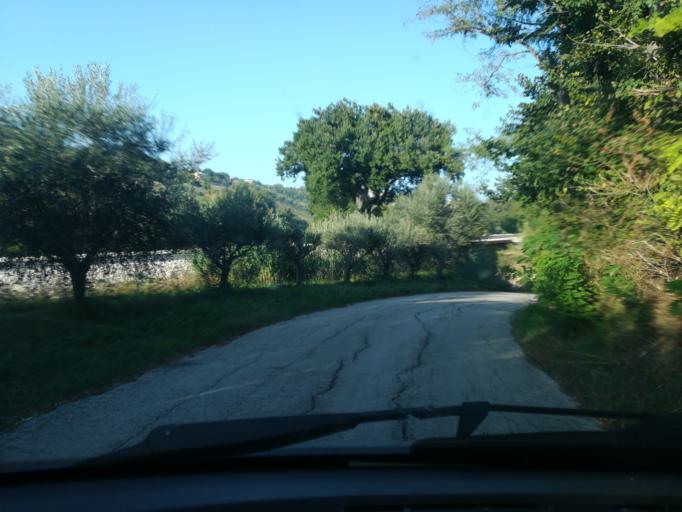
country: IT
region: The Marches
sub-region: Provincia di Macerata
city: Macerata
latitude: 43.2829
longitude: 13.4608
